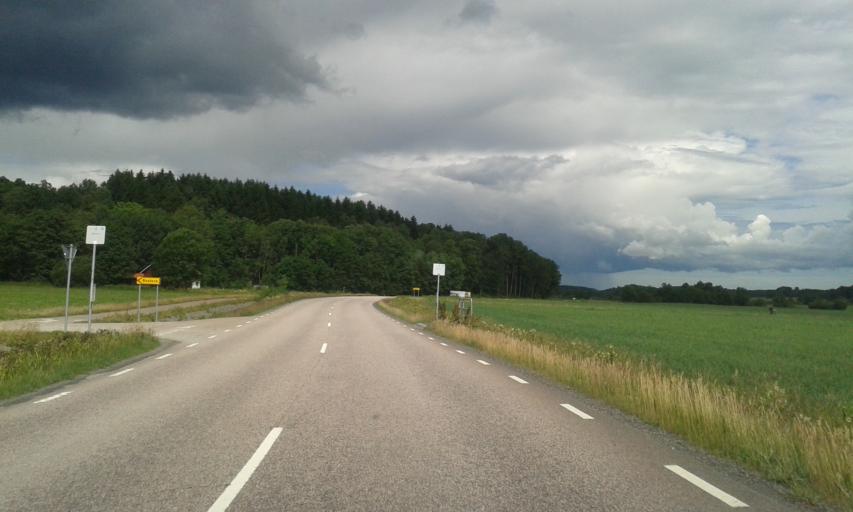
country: SE
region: Vaestra Goetaland
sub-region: Kungalvs Kommun
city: Diserod
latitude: 57.9095
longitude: 12.0108
